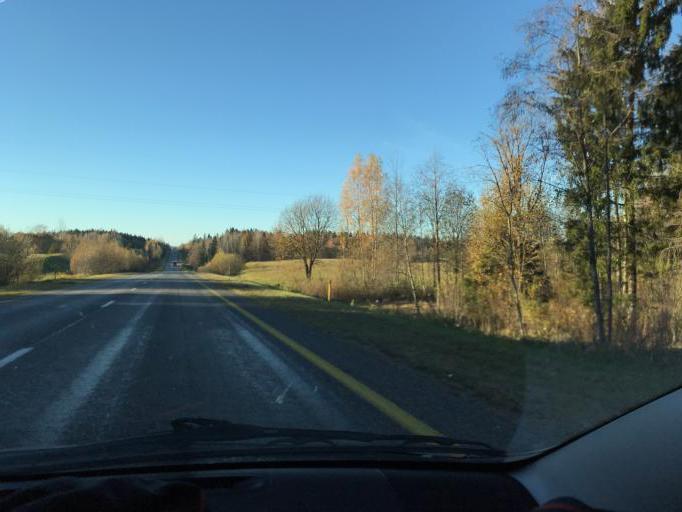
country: BY
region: Vitebsk
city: Vitebsk
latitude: 55.3429
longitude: 30.2270
